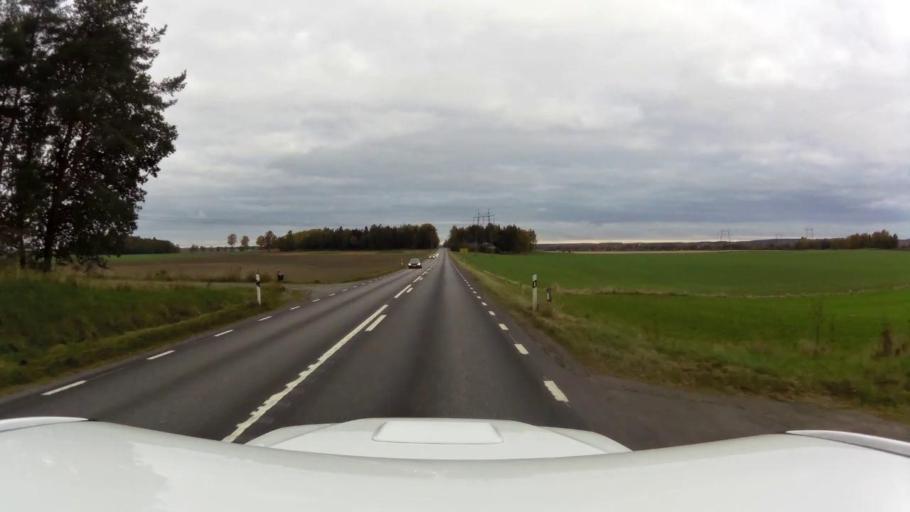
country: SE
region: OEstergoetland
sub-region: Linkopings Kommun
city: Ljungsbro
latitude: 58.5029
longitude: 15.4539
